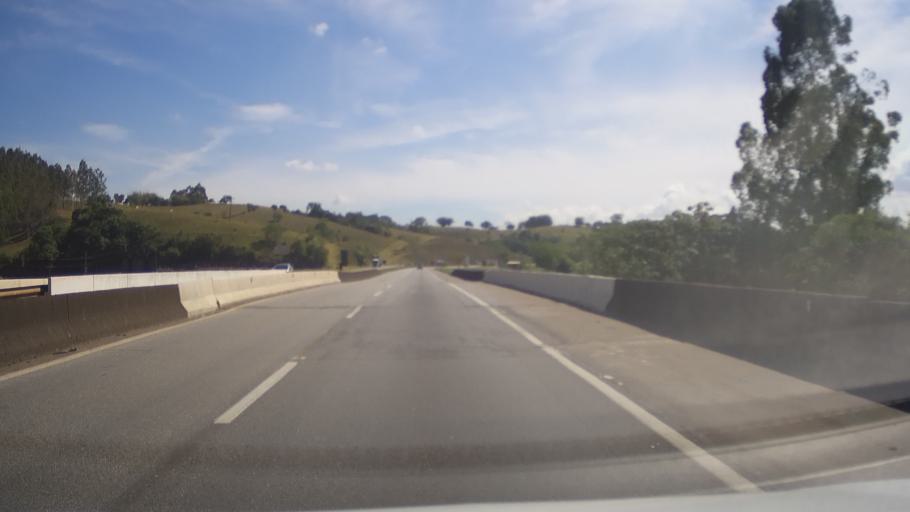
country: BR
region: Minas Gerais
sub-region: Cambui
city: Cambui
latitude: -22.5373
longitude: -46.0363
